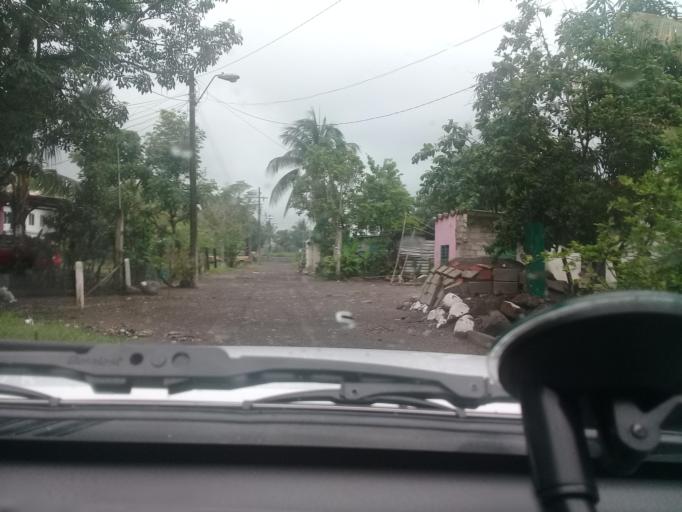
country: MX
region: Veracruz
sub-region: La Antigua
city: Nicolas Blanco (San Pancho)
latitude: 19.3398
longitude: -96.3601
